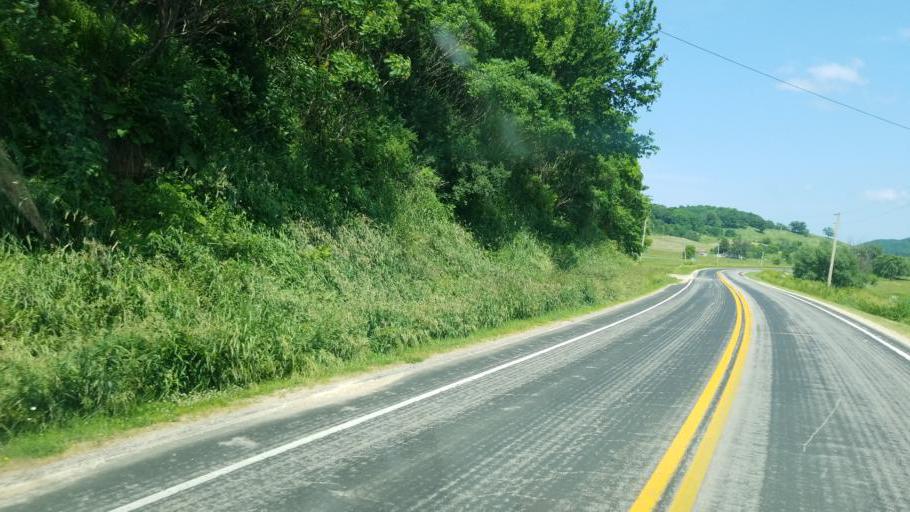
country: US
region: Wisconsin
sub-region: Monroe County
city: Cashton
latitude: 43.5740
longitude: -90.6246
